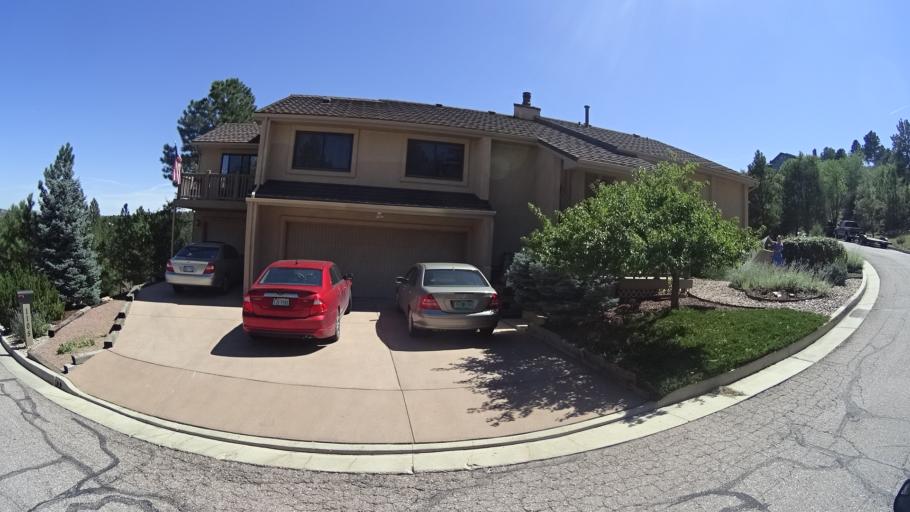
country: US
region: Colorado
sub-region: El Paso County
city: Colorado Springs
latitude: 38.9218
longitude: -104.8067
